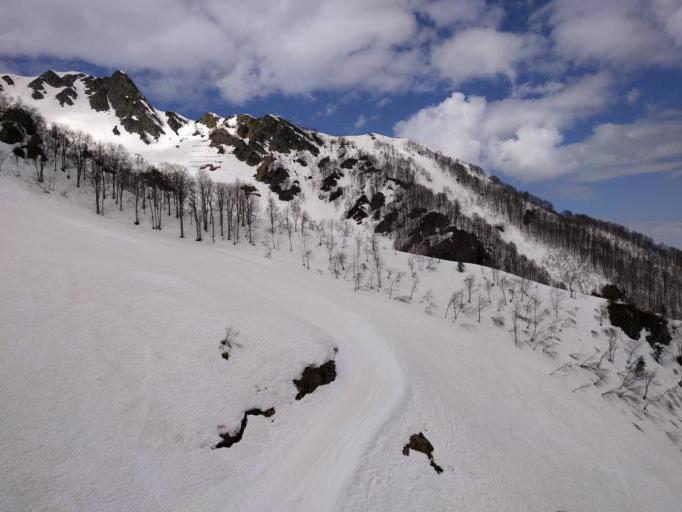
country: RU
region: Krasnodarskiy
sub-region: Sochi City
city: Krasnaya Polyana
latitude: 43.6329
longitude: 40.3121
